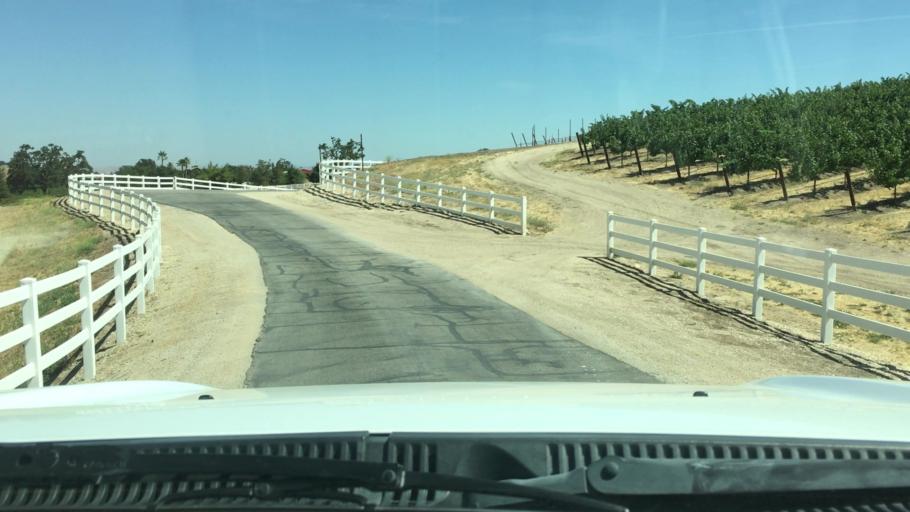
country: US
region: California
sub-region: San Luis Obispo County
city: Paso Robles
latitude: 35.5816
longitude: -120.6044
